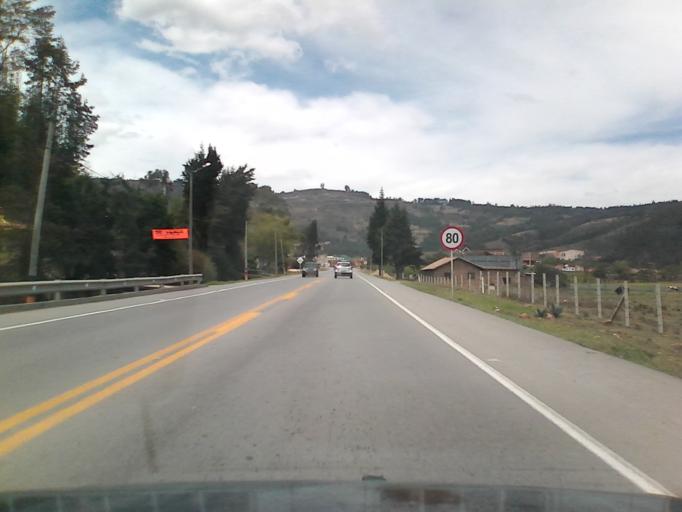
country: CO
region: Boyaca
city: Tibasosa
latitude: 5.7448
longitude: -72.9886
